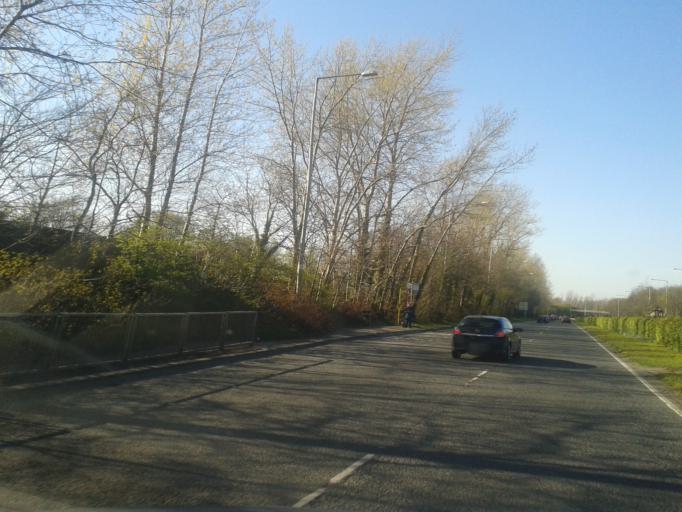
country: IE
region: Leinster
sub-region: Fingal County
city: Swords
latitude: 53.4612
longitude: -6.2131
